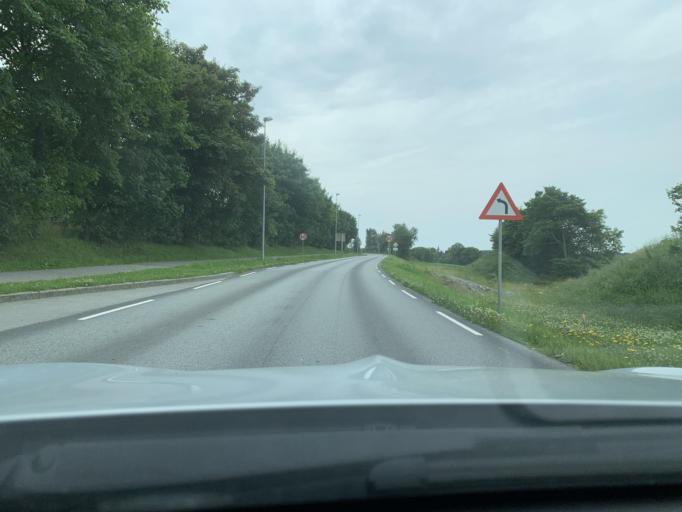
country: NO
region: Rogaland
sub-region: Sandnes
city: Sandnes
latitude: 58.7707
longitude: 5.7235
